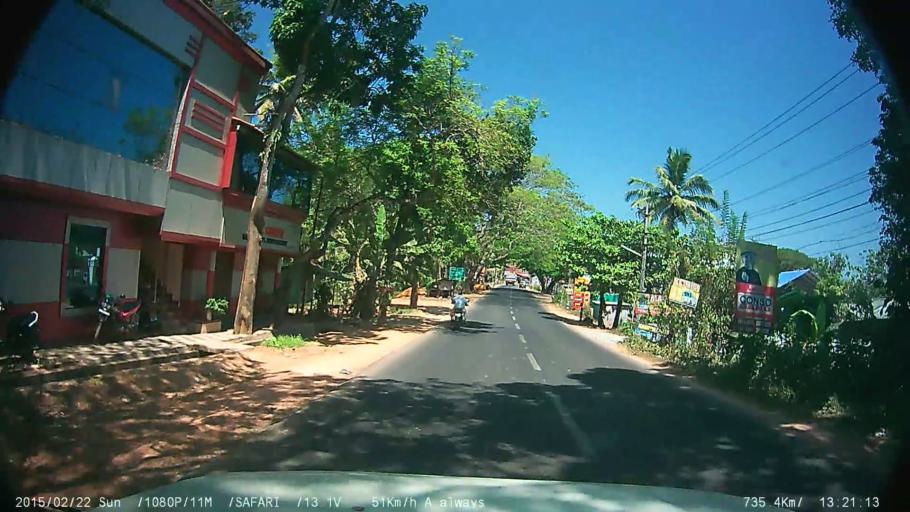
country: IN
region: Kerala
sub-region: Kottayam
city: Changanacheri
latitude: 9.4767
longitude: 76.5806
